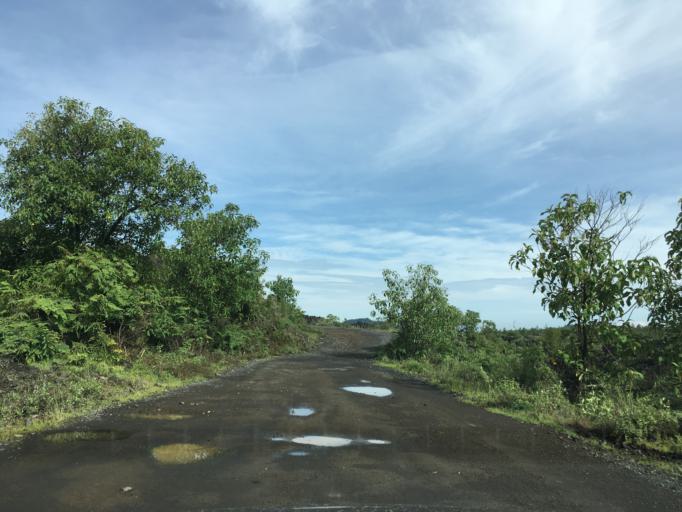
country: MX
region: Michoacan
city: Angahuan
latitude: 19.5217
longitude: -102.2264
